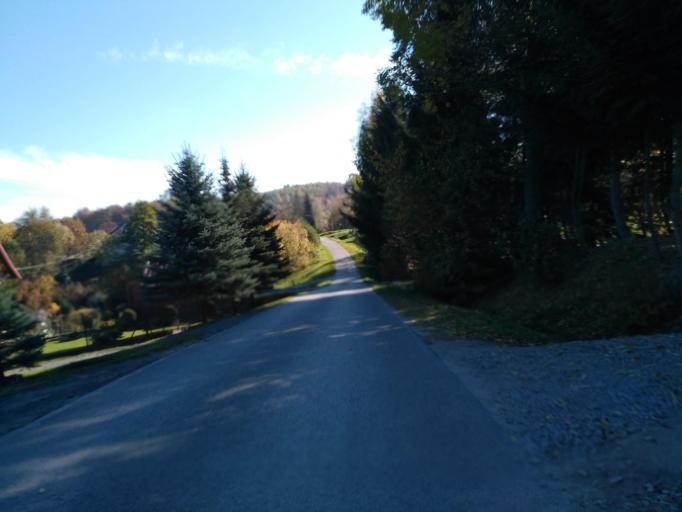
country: PL
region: Subcarpathian Voivodeship
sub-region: Powiat ropczycko-sedziszowski
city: Iwierzyce
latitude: 49.9799
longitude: 21.7274
